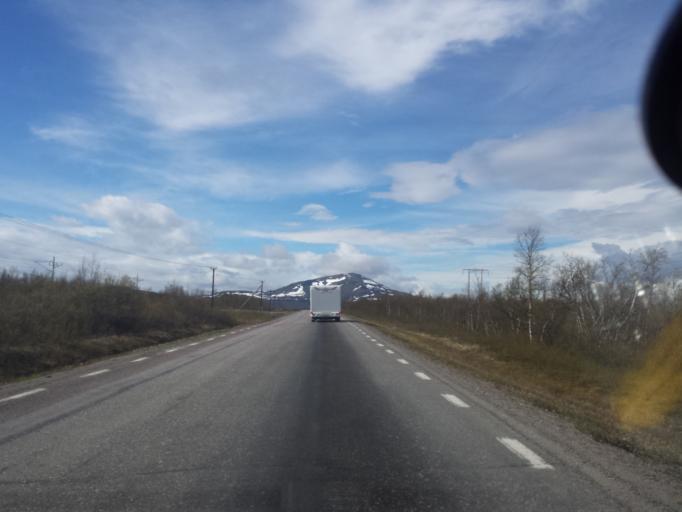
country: SE
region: Norrbotten
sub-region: Kiruna Kommun
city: Kiruna
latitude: 68.1144
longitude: 19.8300
